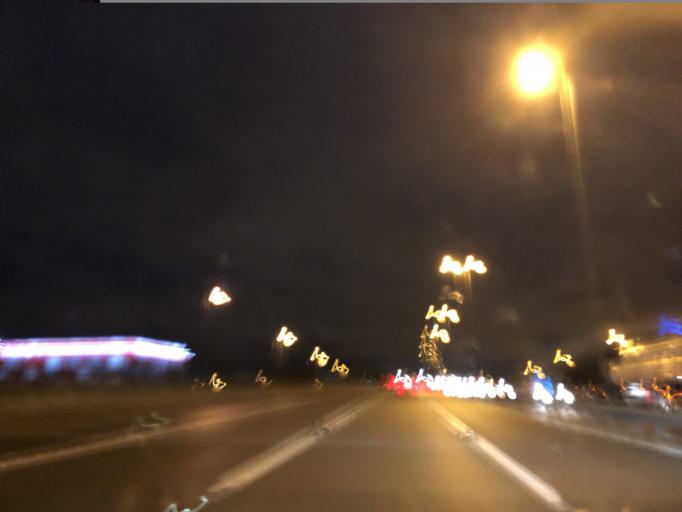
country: GB
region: England
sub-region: Walsall
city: Walsall
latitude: 52.5654
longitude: -1.9993
